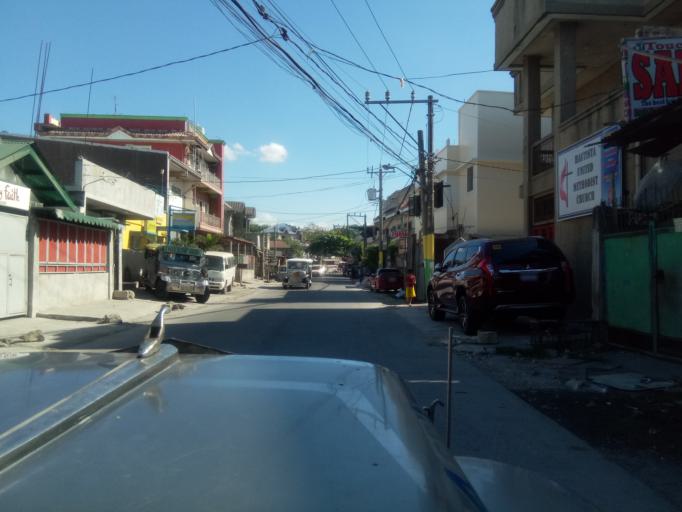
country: PH
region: Calabarzon
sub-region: Province of Cavite
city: Dasmarinas
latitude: 14.3116
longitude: 120.9705
